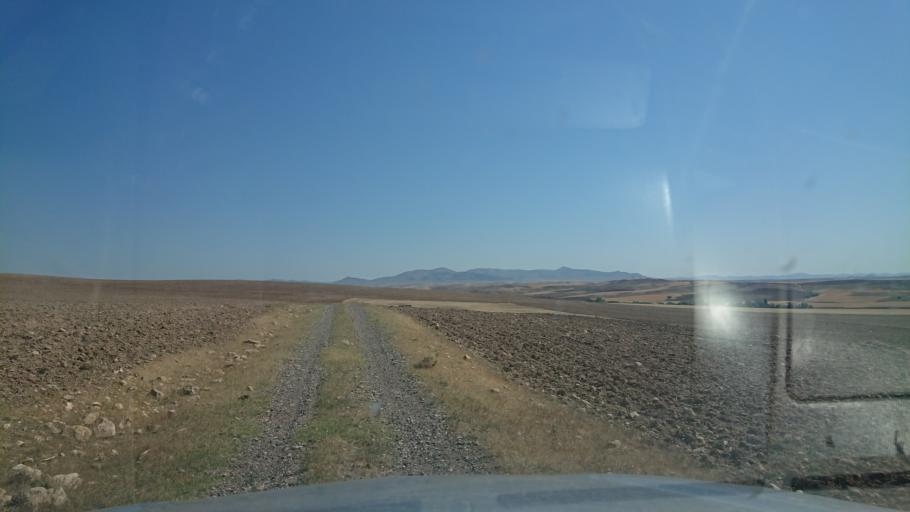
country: TR
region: Aksaray
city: Sariyahsi
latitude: 39.0529
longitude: 33.8891
